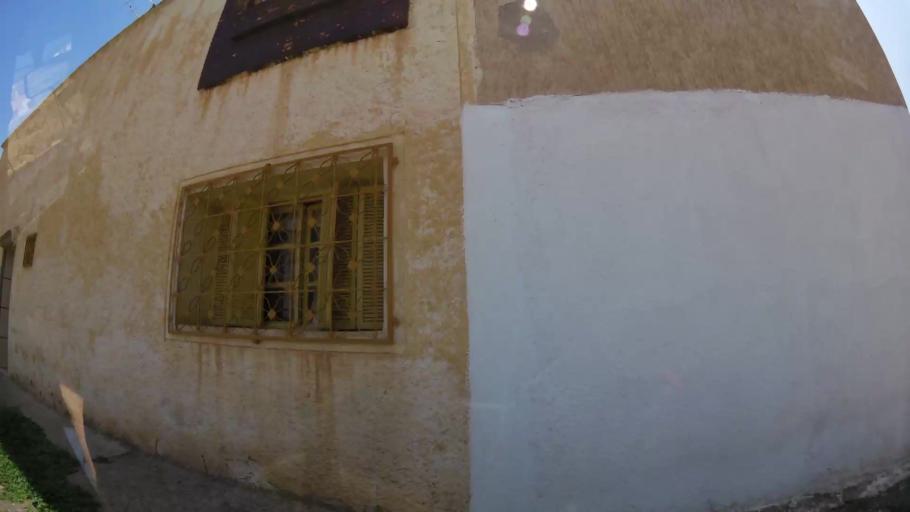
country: MA
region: Oriental
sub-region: Oujda-Angad
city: Oujda
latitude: 34.6893
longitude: -1.8941
